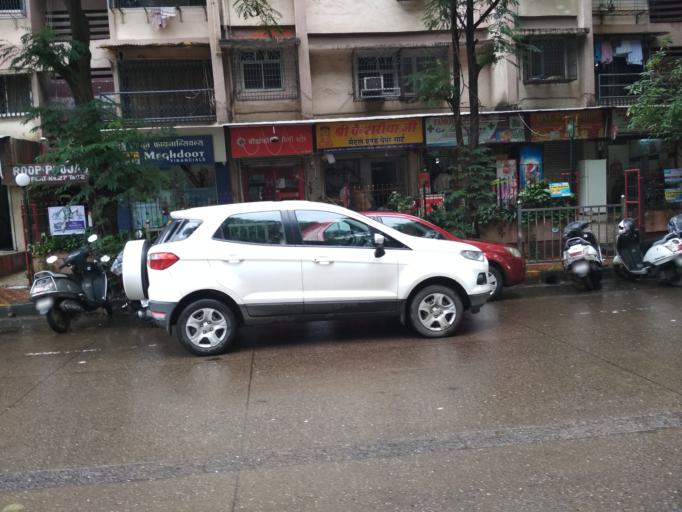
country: IN
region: Maharashtra
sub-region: Thane
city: Thane
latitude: 19.1648
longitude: 72.9439
